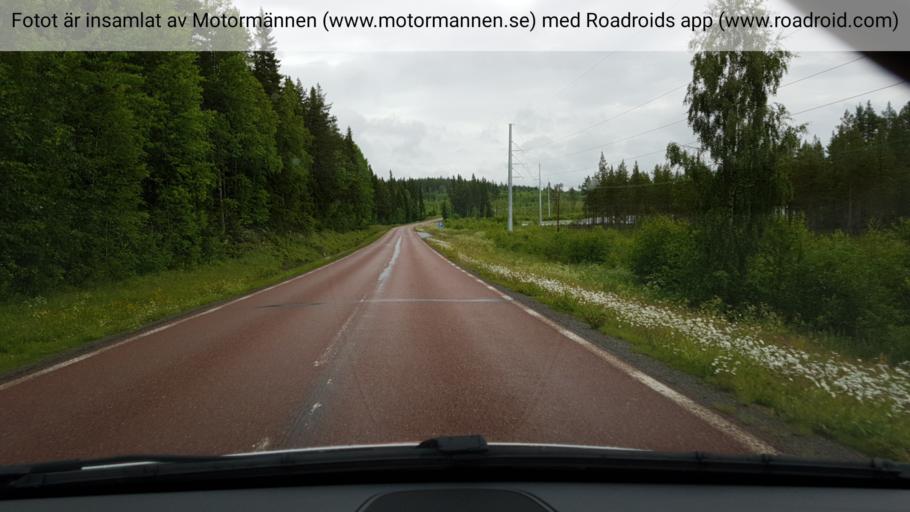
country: SE
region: Vaesterbotten
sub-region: Dorotea Kommun
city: Dorotea
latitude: 64.0585
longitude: 16.0465
